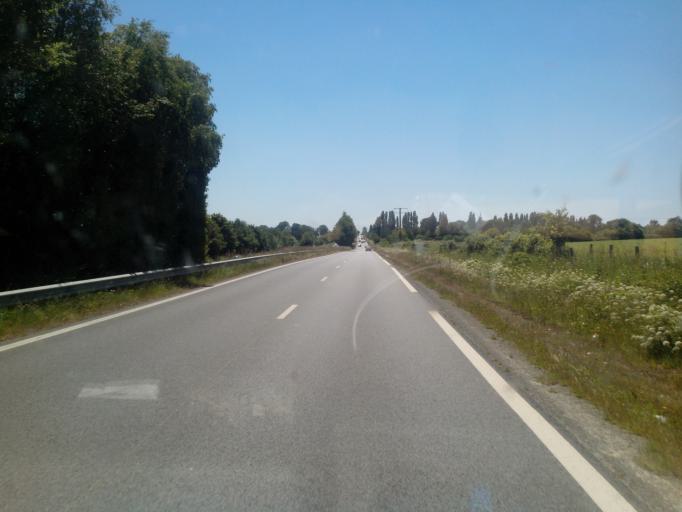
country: FR
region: Brittany
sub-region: Departement d'Ille-et-Vilaine
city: Chevaigne
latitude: 48.2303
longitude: -1.6222
